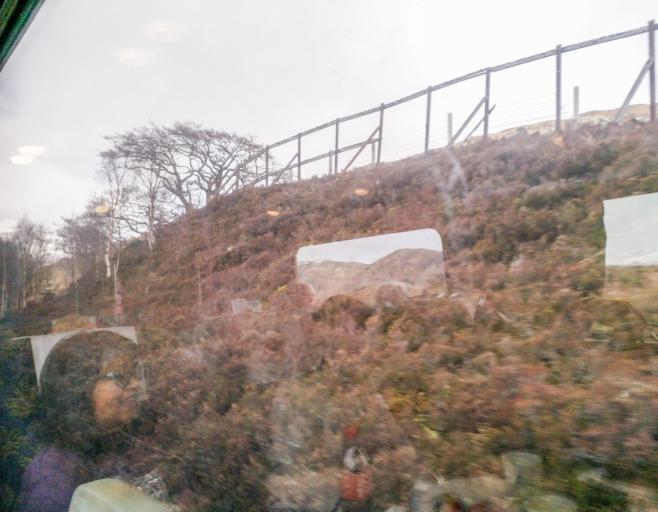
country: GB
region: Scotland
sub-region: Highland
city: Spean Bridge
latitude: 56.7765
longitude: -4.7301
